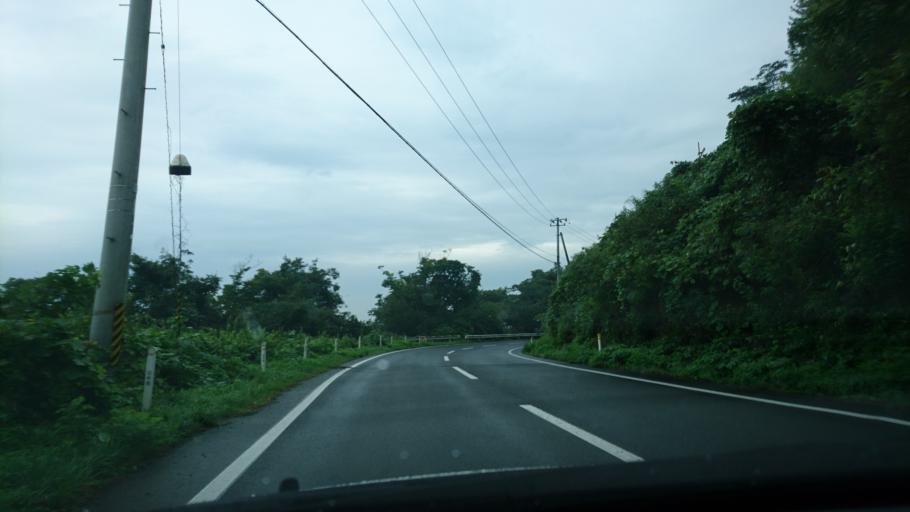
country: JP
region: Iwate
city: Ichinoseki
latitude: 38.8818
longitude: 141.2632
